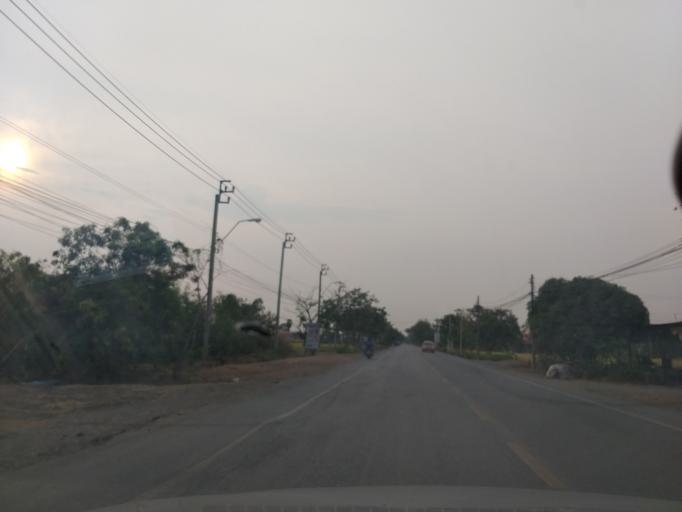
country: TH
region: Bangkok
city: Nong Chok
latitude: 13.8189
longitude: 100.9301
